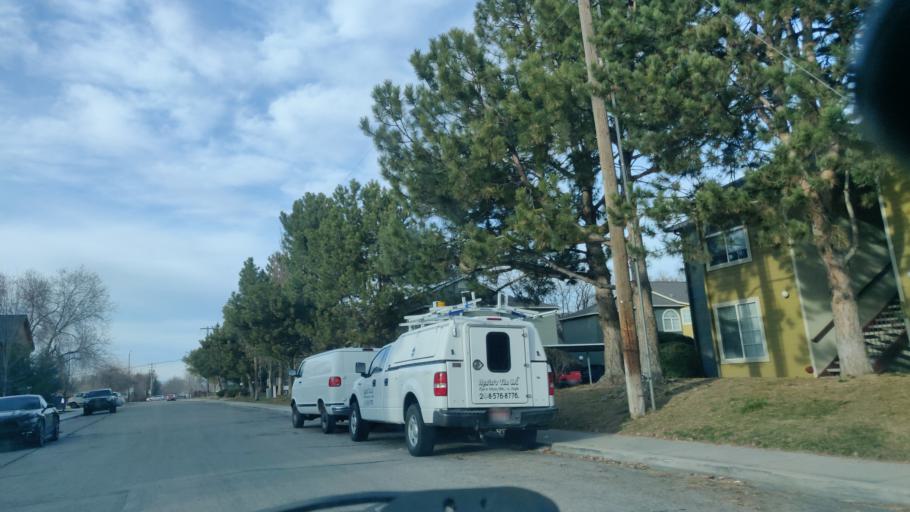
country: US
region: Idaho
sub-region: Ada County
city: Garden City
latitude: 43.6174
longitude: -116.2637
